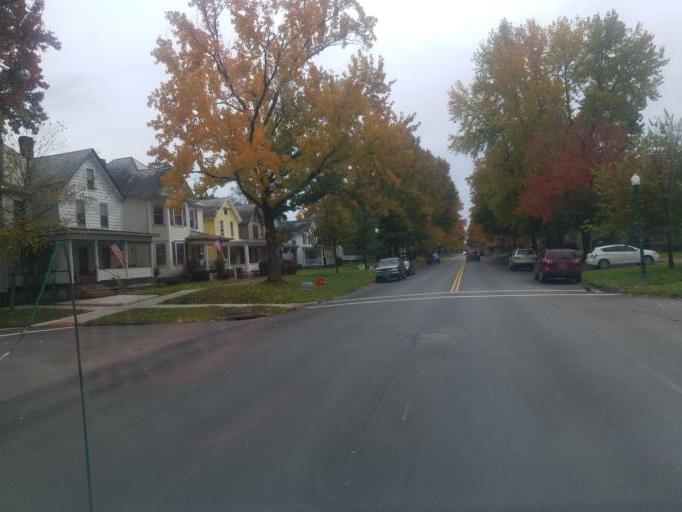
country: US
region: Ohio
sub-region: Washington County
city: Marietta
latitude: 39.4262
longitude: -81.4635
